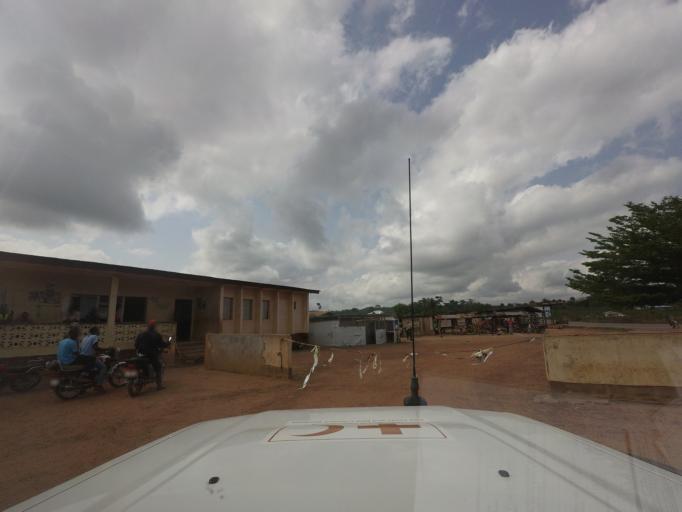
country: LR
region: Nimba
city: Sanniquellie
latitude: 7.2142
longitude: -9.0104
